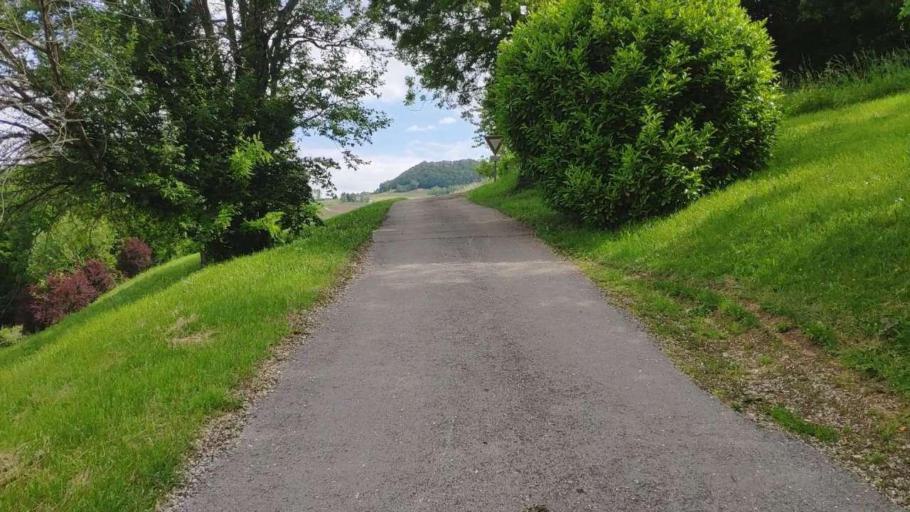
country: FR
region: Franche-Comte
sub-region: Departement du Jura
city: Perrigny
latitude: 46.7567
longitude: 5.6178
